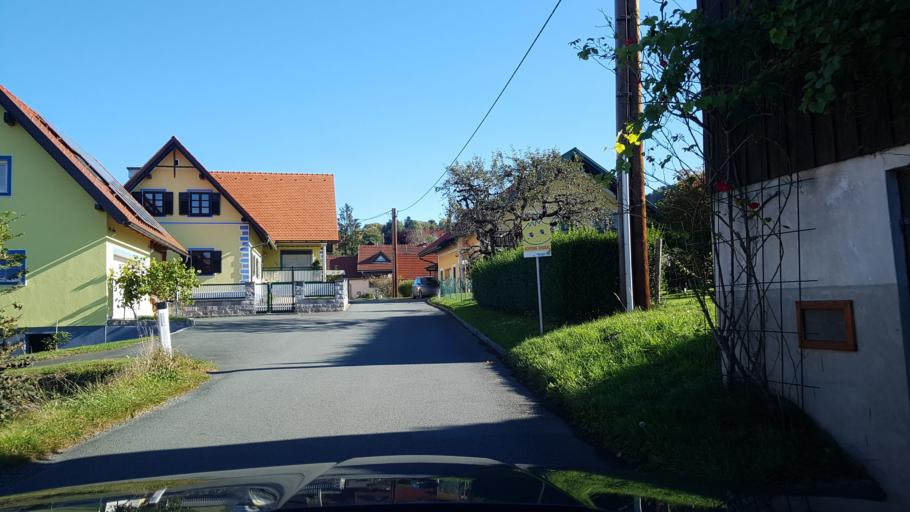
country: AT
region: Styria
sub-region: Politischer Bezirk Leibnitz
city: Kitzeck im Sausal
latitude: 46.7654
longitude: 15.4066
